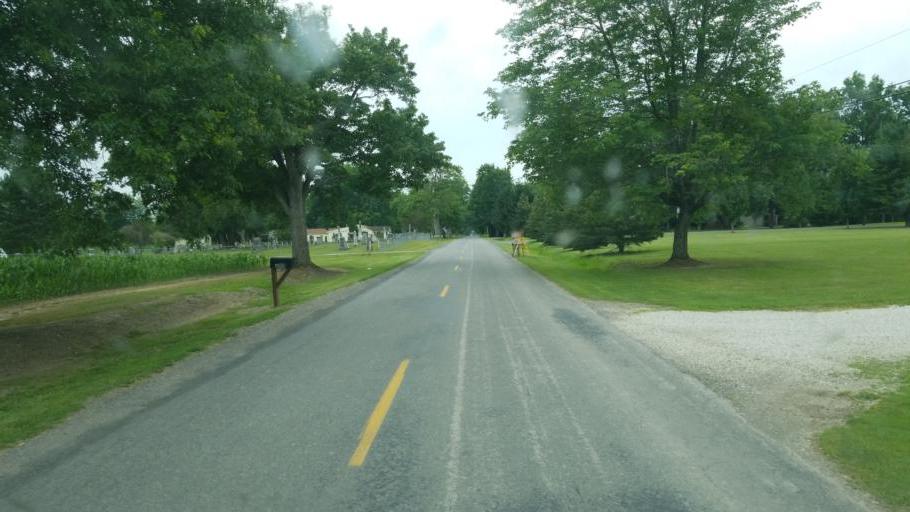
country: US
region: Ohio
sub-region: Trumbull County
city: Cortland
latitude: 41.4008
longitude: -80.7768
